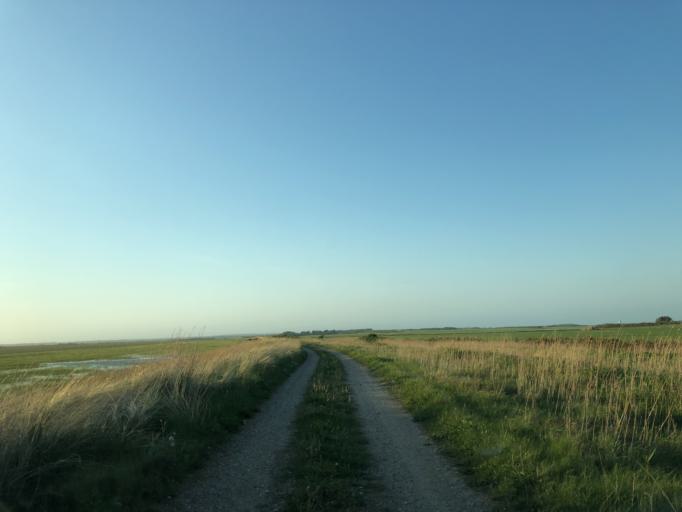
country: DK
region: Central Jutland
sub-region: Ringkobing-Skjern Kommune
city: Ringkobing
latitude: 56.2147
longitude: 8.1647
